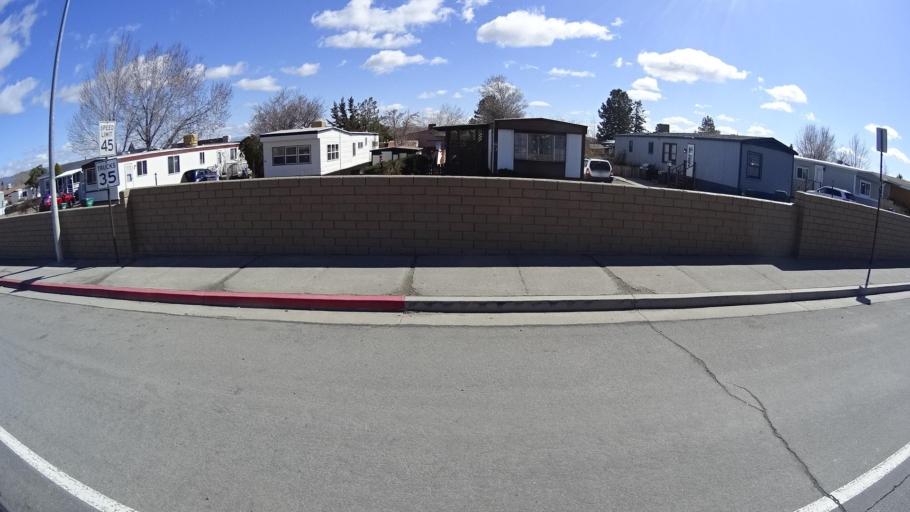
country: US
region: Nevada
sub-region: Washoe County
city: Lemmon Valley
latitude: 39.6263
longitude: -119.8820
